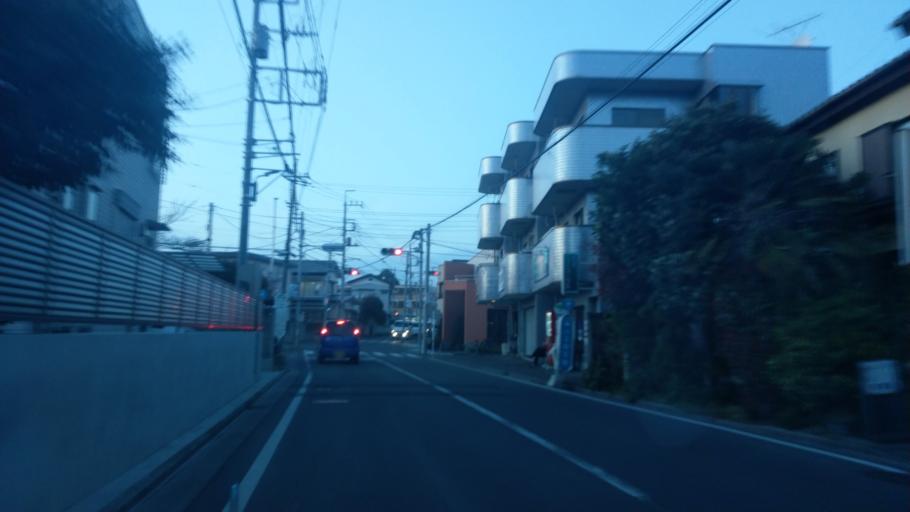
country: JP
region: Saitama
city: Yono
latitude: 35.8807
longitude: 139.6045
